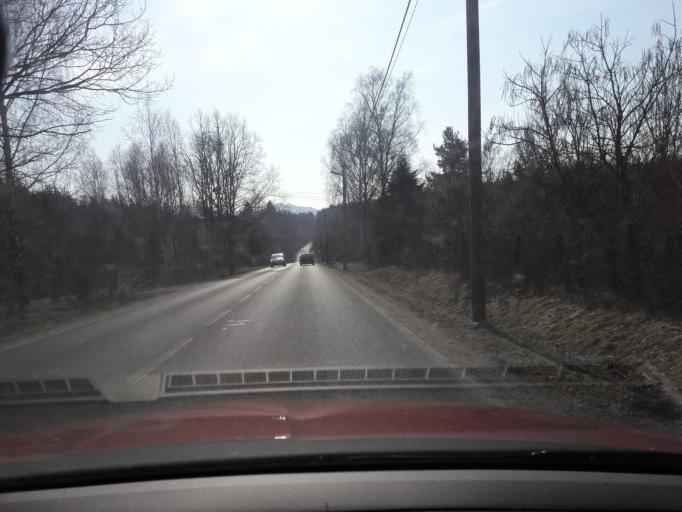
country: CZ
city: Novy Bor
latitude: 50.7548
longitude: 14.5627
